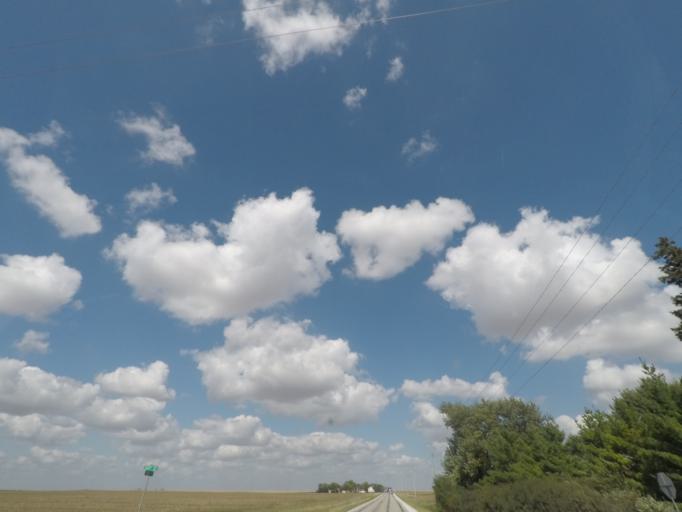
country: US
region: Iowa
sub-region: Story County
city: Nevada
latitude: 42.0633
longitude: -93.4056
